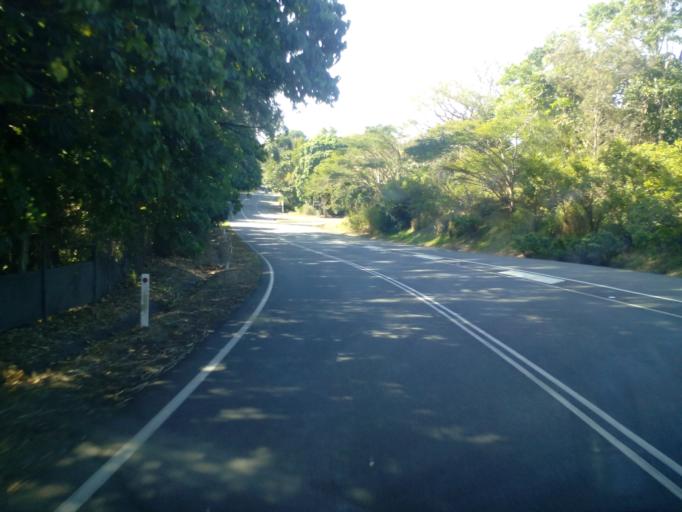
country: AU
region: New South Wales
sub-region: Tweed
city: Kingscliff
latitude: -28.2616
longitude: 153.5706
